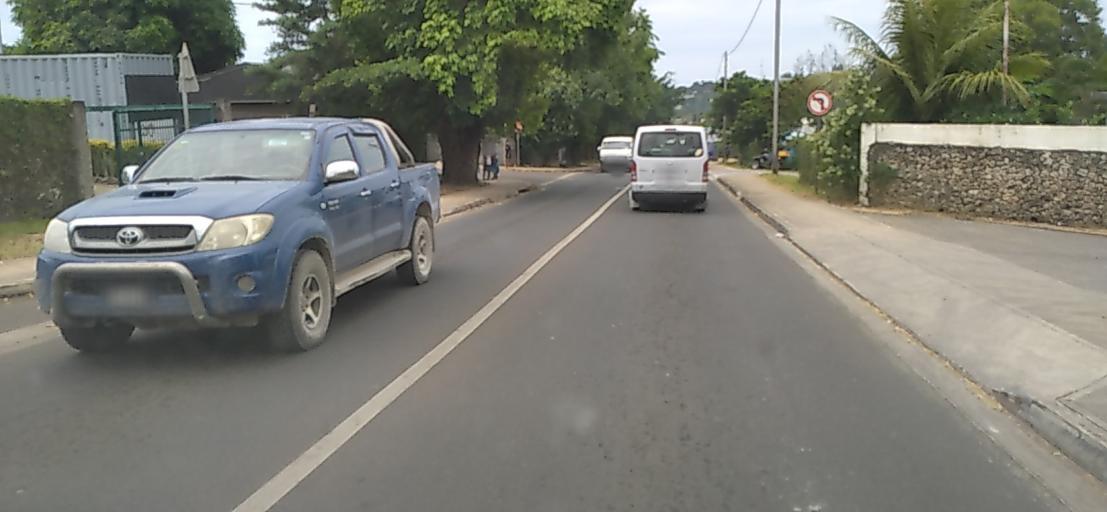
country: VU
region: Shefa
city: Port-Vila
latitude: -17.7386
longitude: 168.3199
